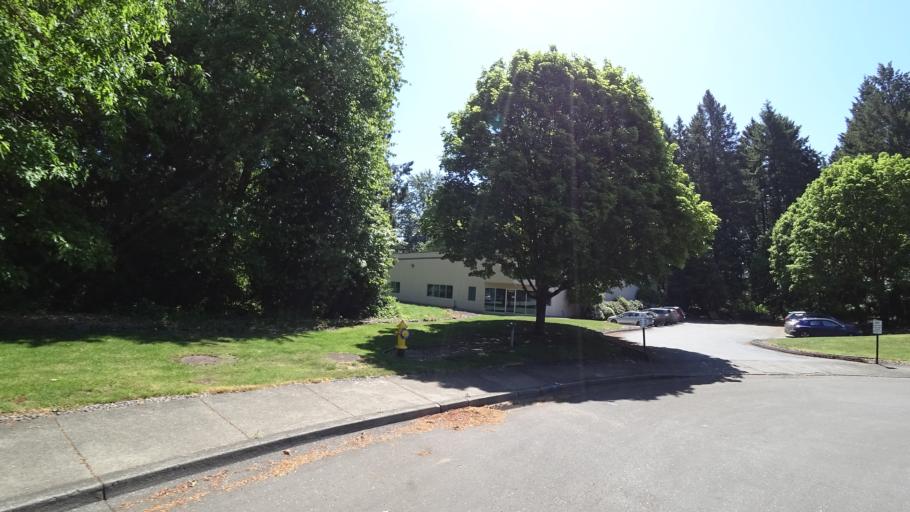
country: US
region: Oregon
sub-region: Washington County
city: Rockcreek
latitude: 45.5267
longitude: -122.9236
